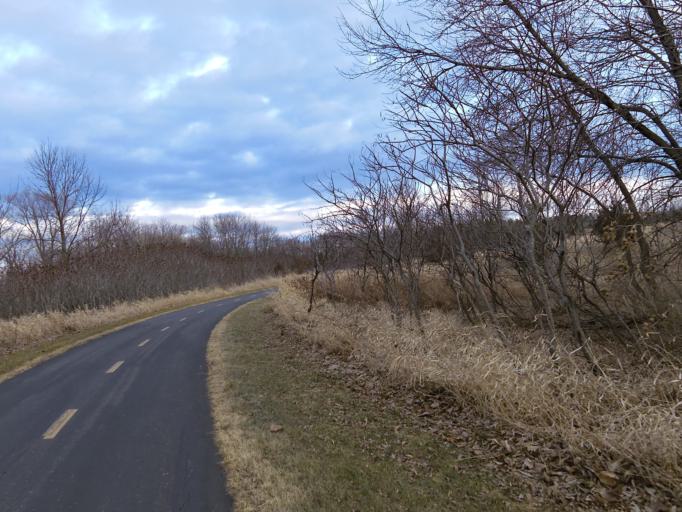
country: US
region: Minnesota
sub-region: Scott County
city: Prior Lake
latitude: 44.6907
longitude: -93.3984
